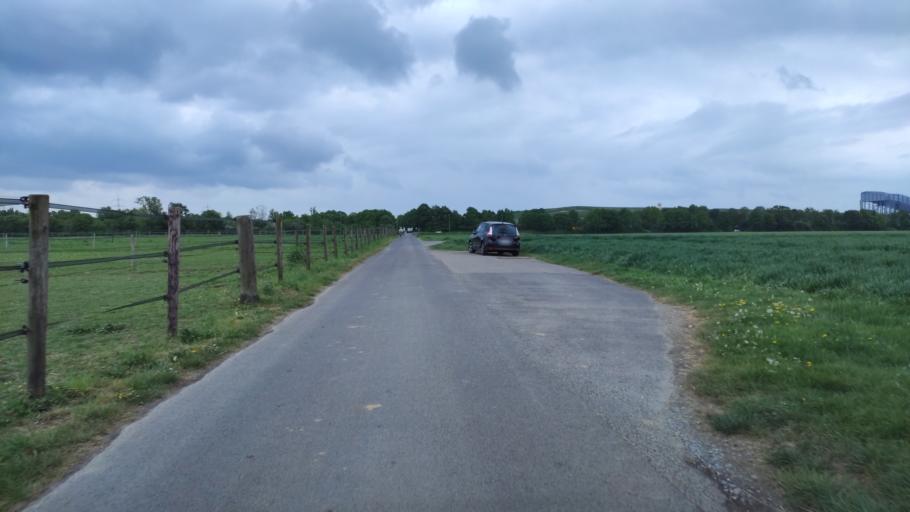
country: DE
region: North Rhine-Westphalia
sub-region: Regierungsbezirk Dusseldorf
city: Neuss
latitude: 51.1840
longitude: 6.6540
